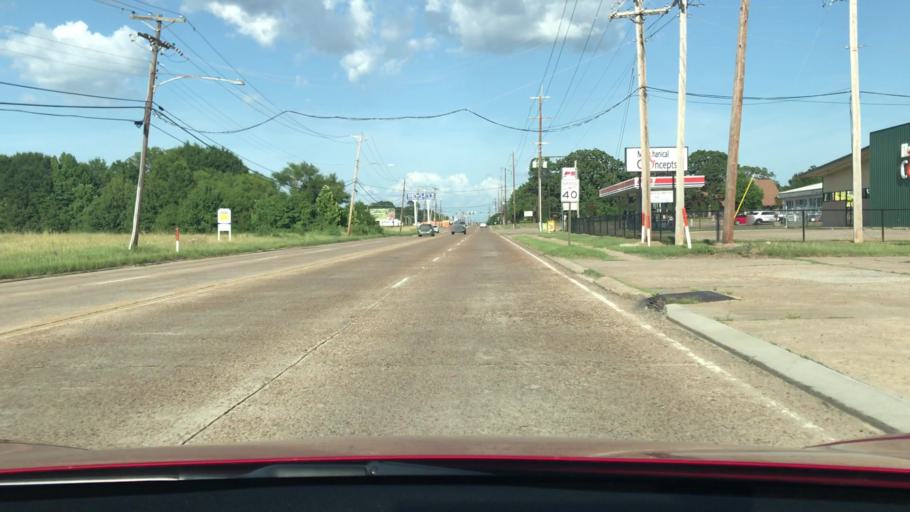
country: US
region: Louisiana
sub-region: Bossier Parish
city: Bossier City
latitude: 32.4420
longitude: -93.7783
